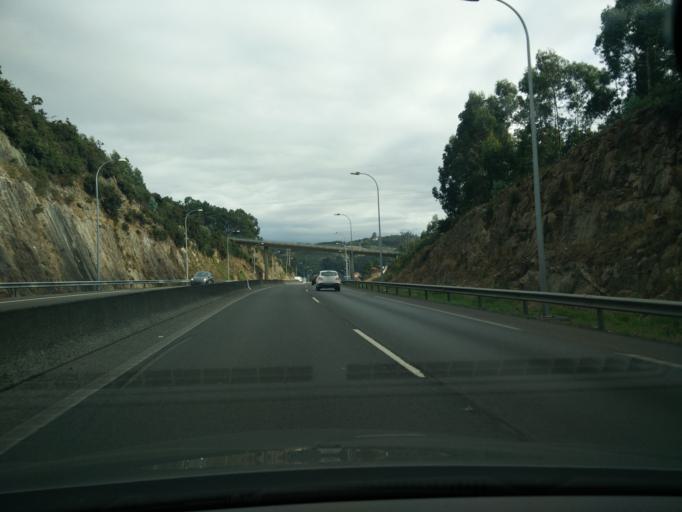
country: ES
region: Galicia
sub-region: Provincia da Coruna
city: Culleredo
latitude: 43.3229
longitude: -8.3927
